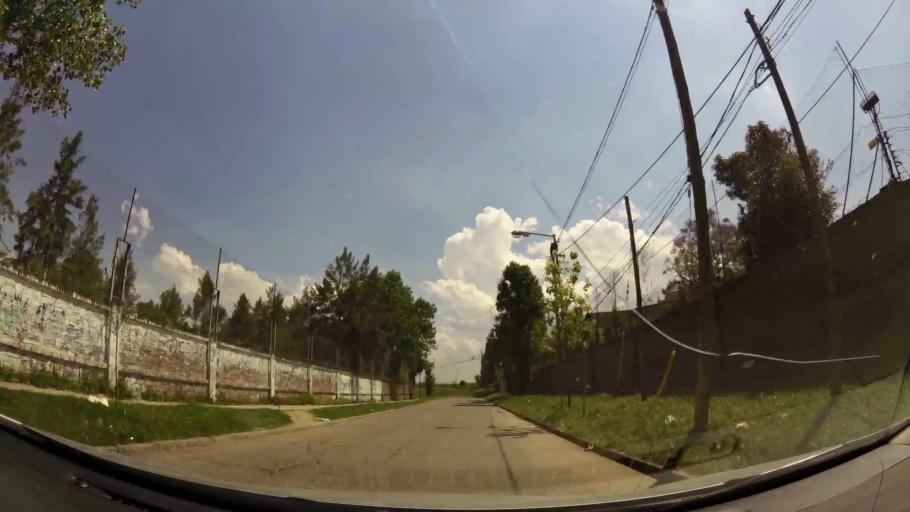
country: AR
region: Buenos Aires
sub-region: Partido de Tigre
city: Tigre
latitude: -34.4612
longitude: -58.5830
